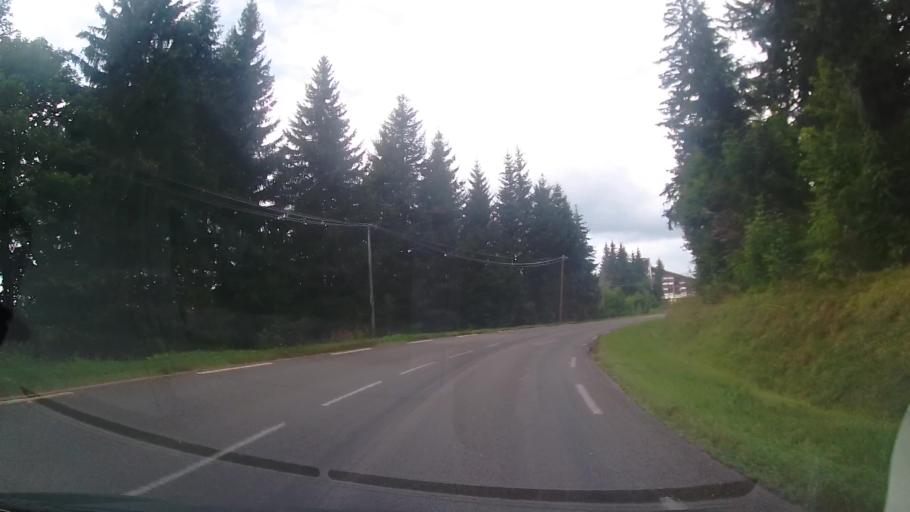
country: FR
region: Franche-Comte
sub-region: Departement du Jura
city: Les Rousses
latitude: 46.4602
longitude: 6.0724
